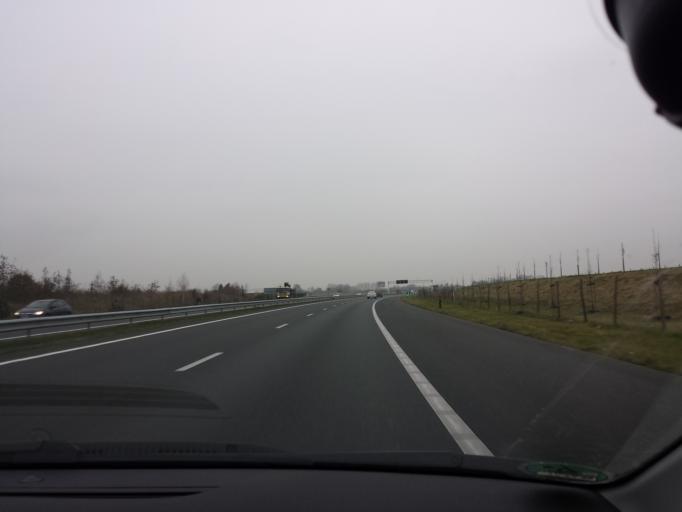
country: NL
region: Limburg
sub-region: Gemeente Roermond
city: Leeuwen
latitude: 51.2199
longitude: 6.0195
